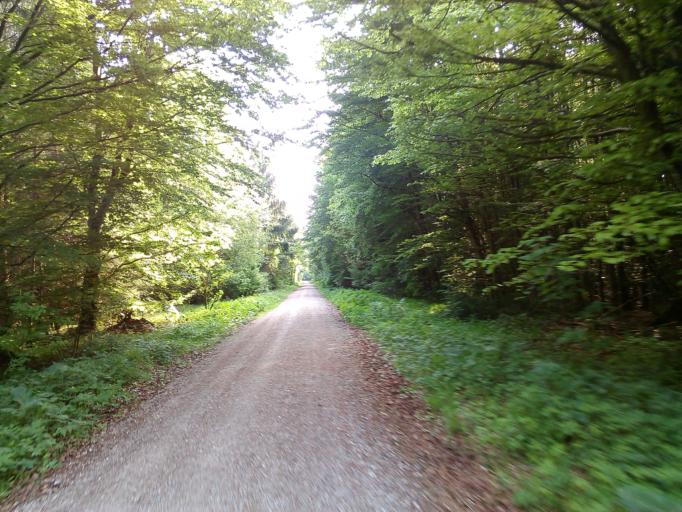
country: DE
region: Bavaria
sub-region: Upper Bavaria
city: Gauting
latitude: 48.0776
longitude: 11.3644
